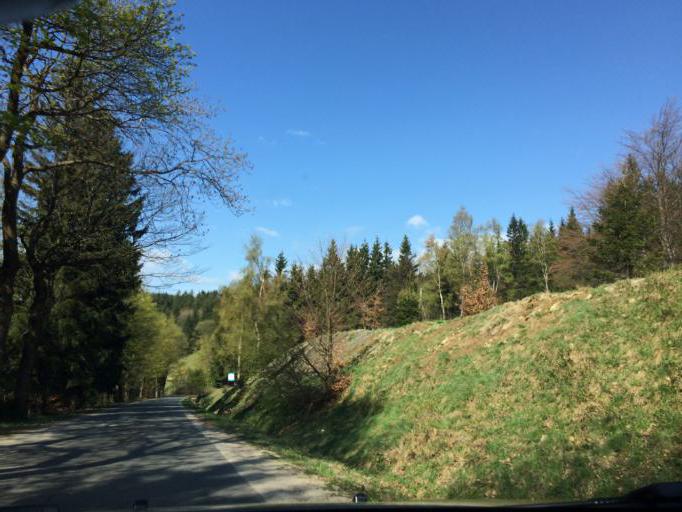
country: PL
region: Lower Silesian Voivodeship
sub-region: Powiat klodzki
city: Jugow
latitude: 50.6553
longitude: 16.5248
